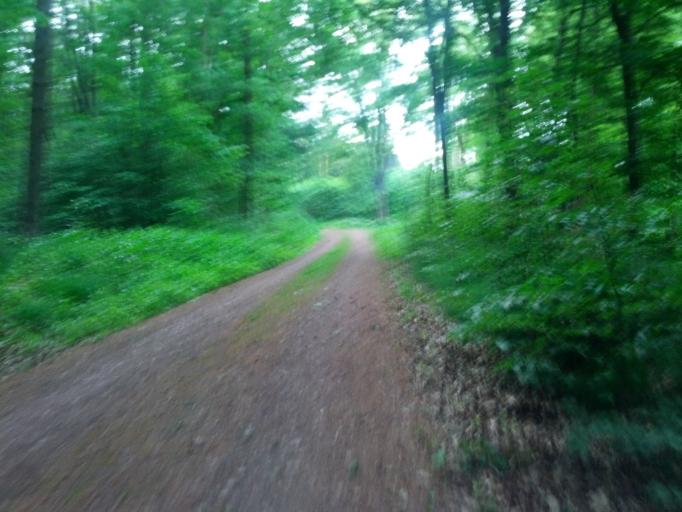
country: DE
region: Thuringia
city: Eisenach
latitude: 50.9553
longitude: 10.3425
